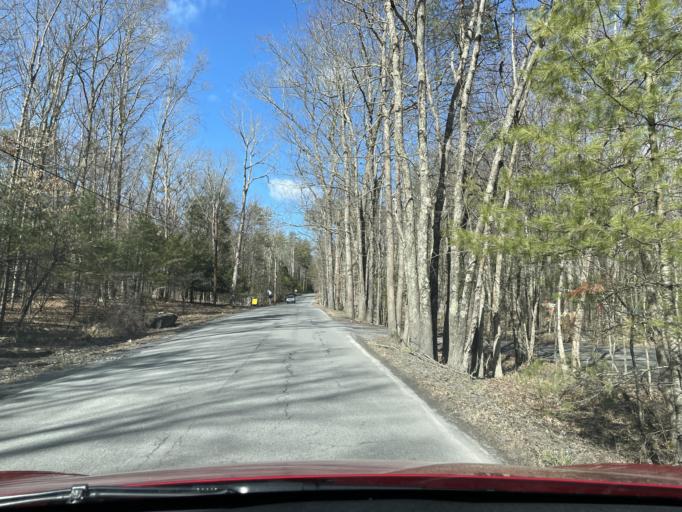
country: US
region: New York
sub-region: Ulster County
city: Zena
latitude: 42.0365
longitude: -74.0684
